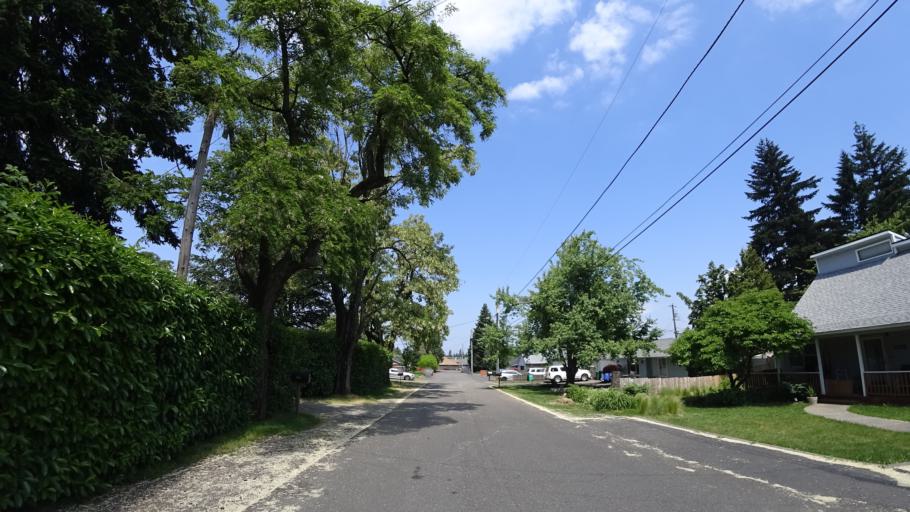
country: US
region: Oregon
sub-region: Multnomah County
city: Fairview
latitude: 45.5360
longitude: -122.5038
